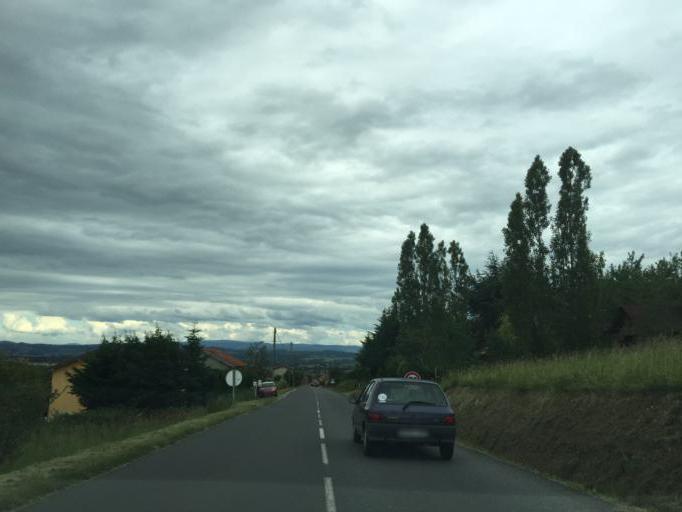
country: FR
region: Rhone-Alpes
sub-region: Departement de la Loire
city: Saint-Marcellin-en-Forez
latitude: 45.5070
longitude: 4.1346
